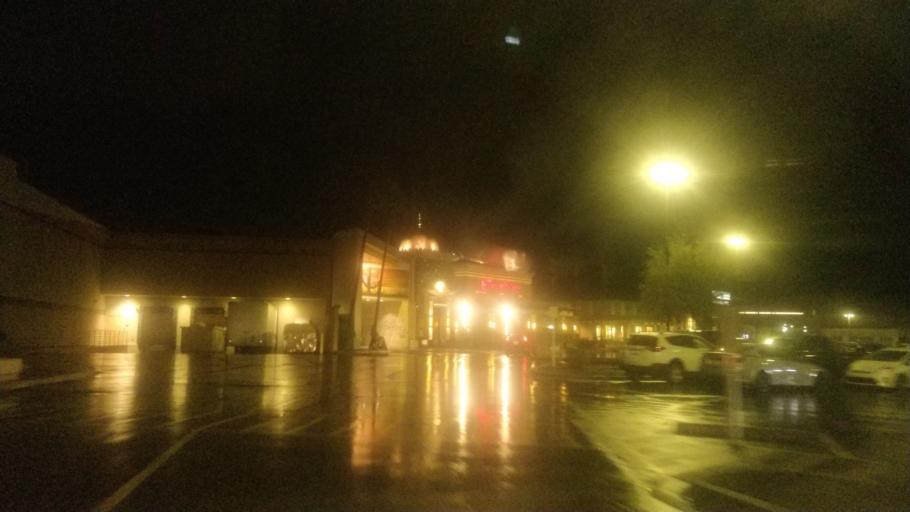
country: US
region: Arizona
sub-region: Maricopa County
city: Chandler
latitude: 33.3027
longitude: -111.8972
